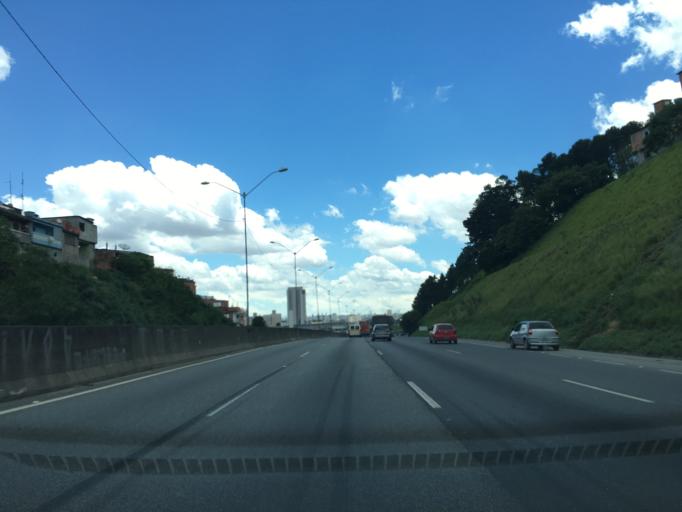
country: BR
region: Sao Paulo
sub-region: Guarulhos
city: Guarulhos
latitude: -23.4396
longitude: -46.5680
